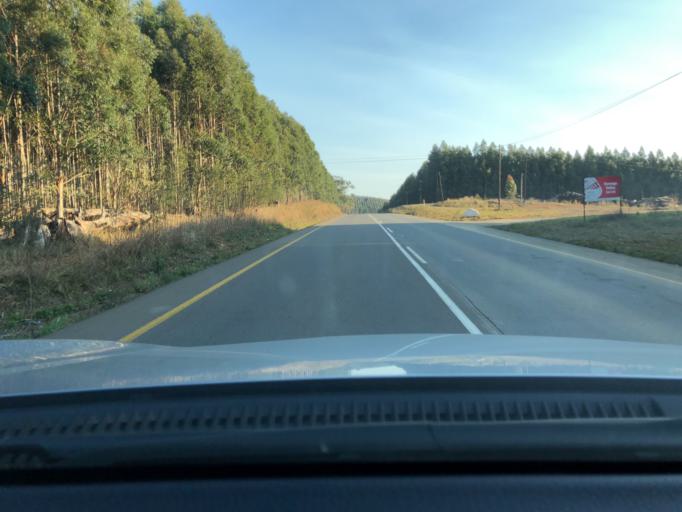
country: ZA
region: KwaZulu-Natal
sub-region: Sisonke District Municipality
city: Ixopo
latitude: -30.1820
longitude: 30.0588
